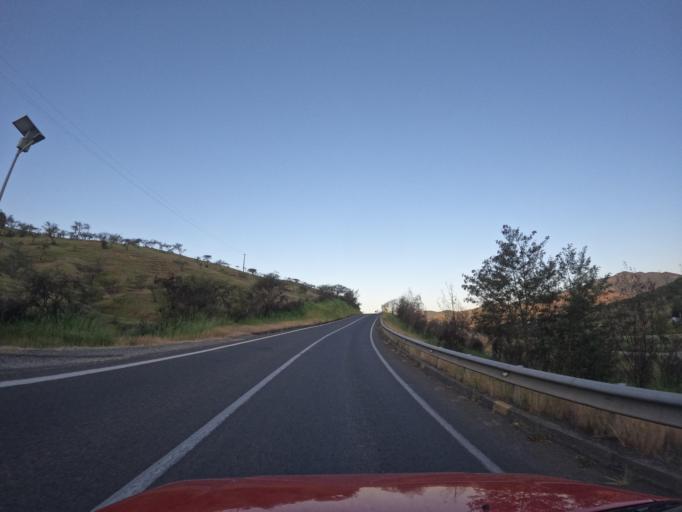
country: CL
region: Maule
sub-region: Provincia de Curico
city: Rauco
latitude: -35.0774
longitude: -71.6298
